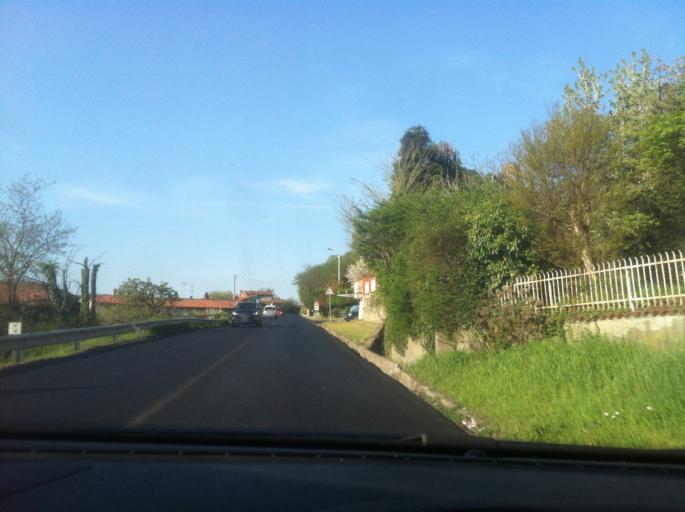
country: IT
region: Piedmont
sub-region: Provincia di Torino
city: Candia Canavese
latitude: 45.3304
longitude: 7.8854
